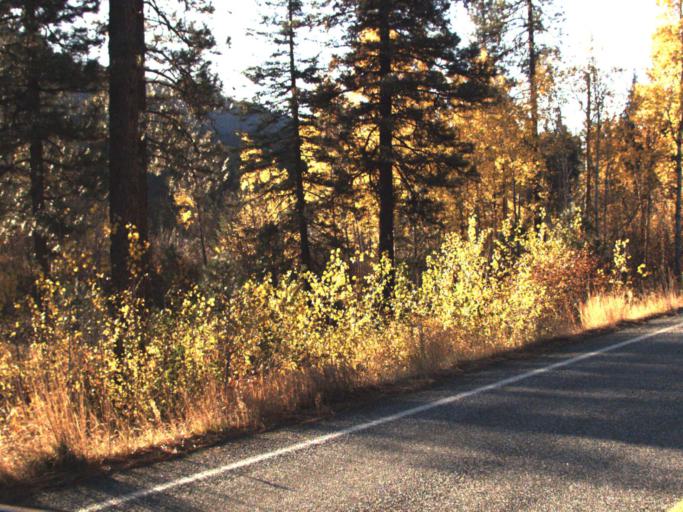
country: US
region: Washington
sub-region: Okanogan County
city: Coulee Dam
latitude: 48.2037
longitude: -118.7138
